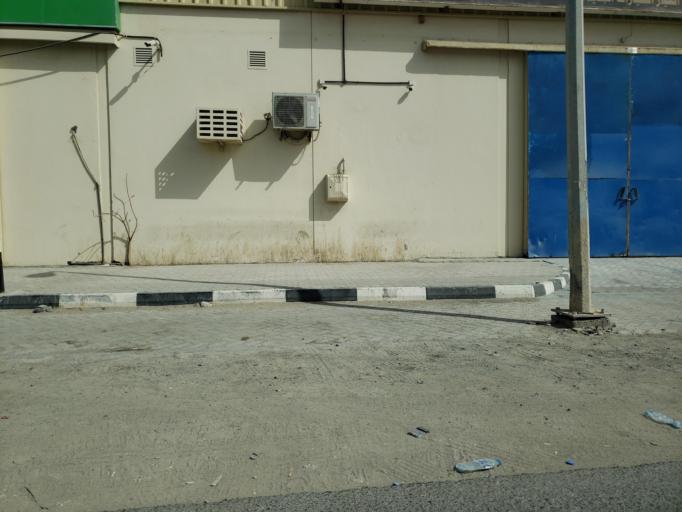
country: AE
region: Ash Shariqah
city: Sharjah
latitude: 25.3285
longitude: 55.4015
